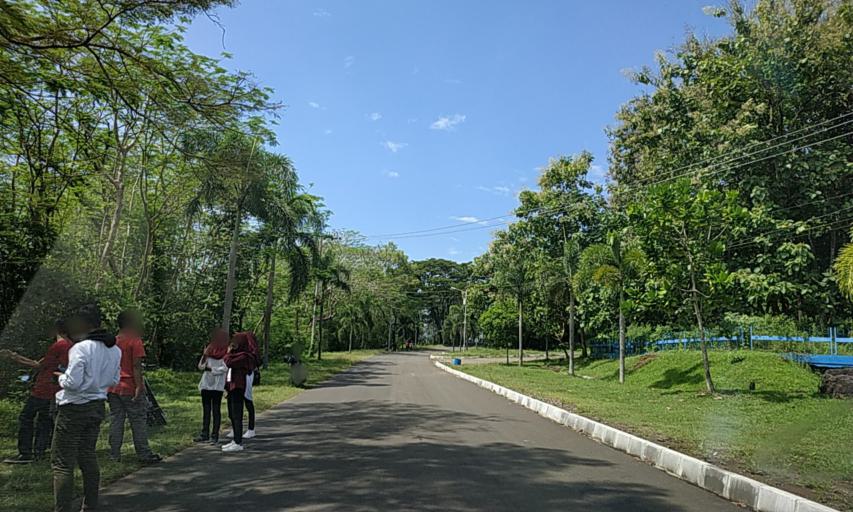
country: ID
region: Central Java
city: Selogiri
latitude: -7.8369
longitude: 110.9241
